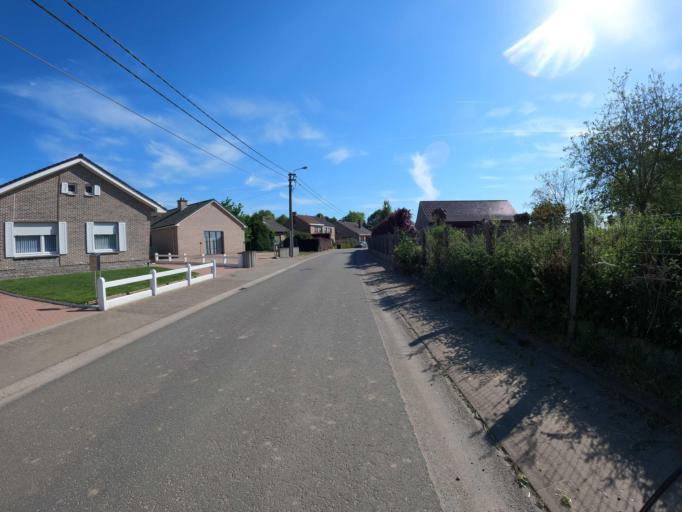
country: BE
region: Flanders
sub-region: Provincie Oost-Vlaanderen
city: Oosterzele
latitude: 50.9224
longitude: 3.7842
